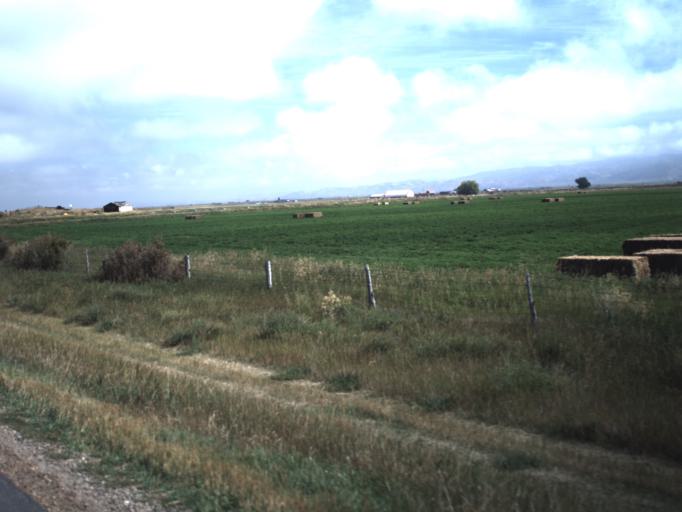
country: US
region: Utah
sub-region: Rich County
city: Randolph
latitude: 41.6773
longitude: -111.1846
